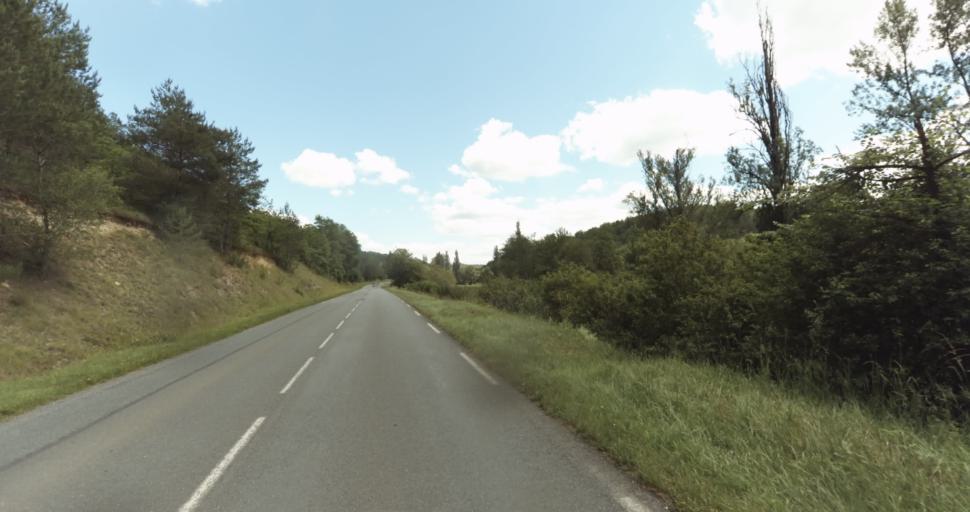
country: FR
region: Aquitaine
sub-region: Departement de la Dordogne
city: Lalinde
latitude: 44.8486
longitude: 0.8154
